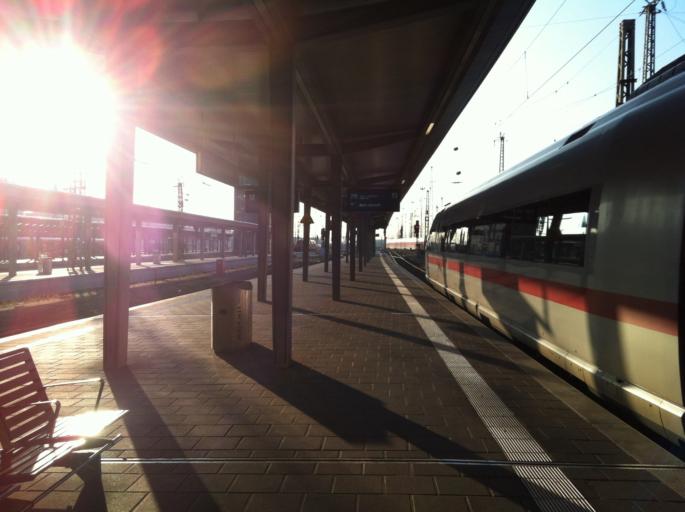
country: DE
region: Hesse
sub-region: Regierungsbezirk Darmstadt
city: Frankfurt am Main
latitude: 50.1061
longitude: 8.6612
